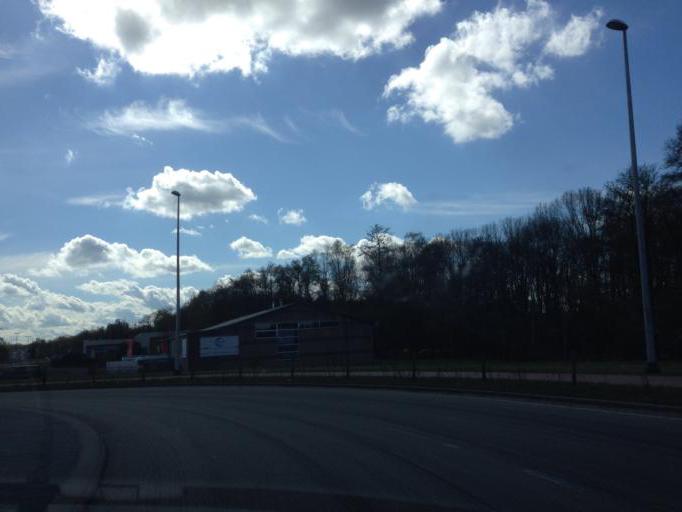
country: BE
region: Flanders
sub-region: Provincie Limburg
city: Genk
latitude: 50.9215
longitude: 5.4841
